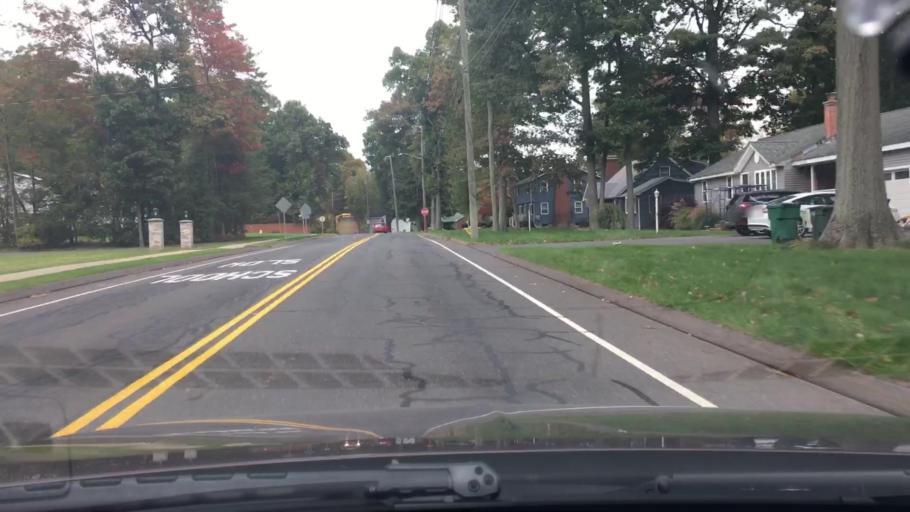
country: US
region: Connecticut
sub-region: Hartford County
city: Manchester
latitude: 41.8293
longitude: -72.5291
